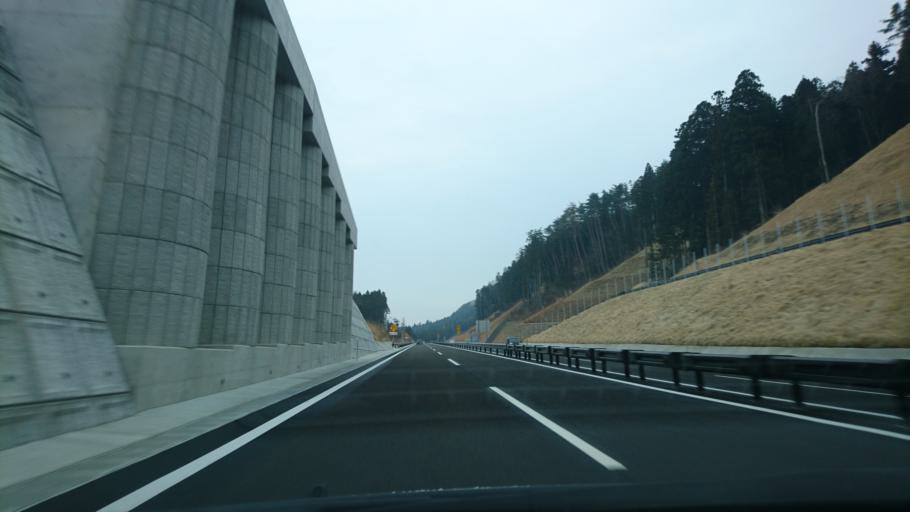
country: JP
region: Iwate
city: Ofunato
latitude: 38.9805
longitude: 141.6177
